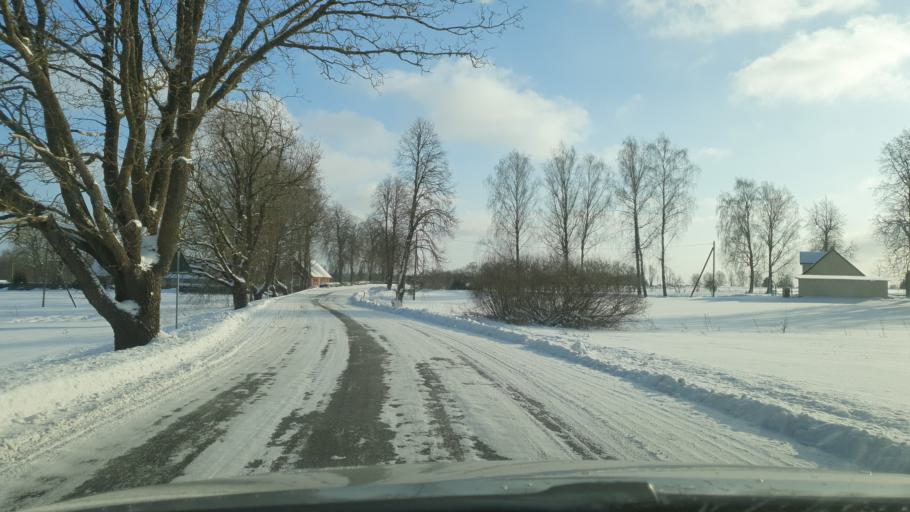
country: EE
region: Valgamaa
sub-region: Torva linn
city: Torva
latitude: 58.1365
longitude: 25.8061
